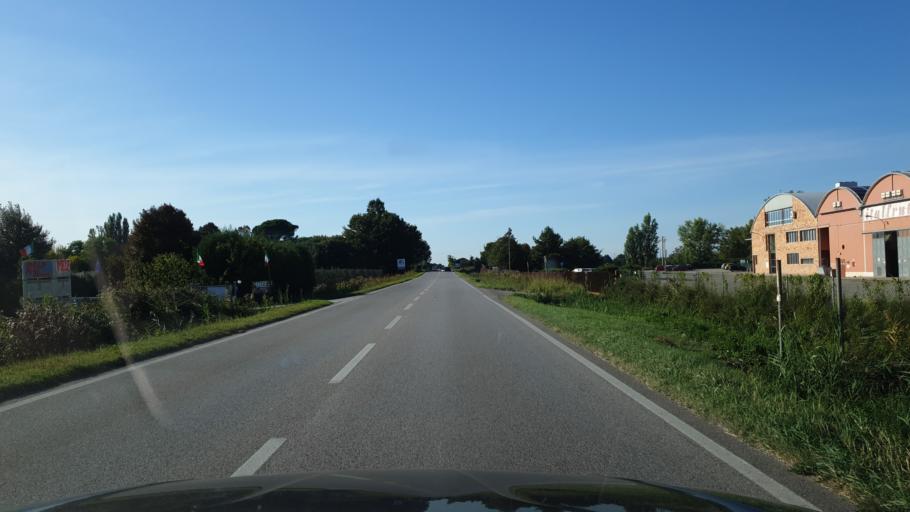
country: IT
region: Emilia-Romagna
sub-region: Provincia di Ravenna
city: Fornace Zarattini
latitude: 44.4329
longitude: 12.1483
